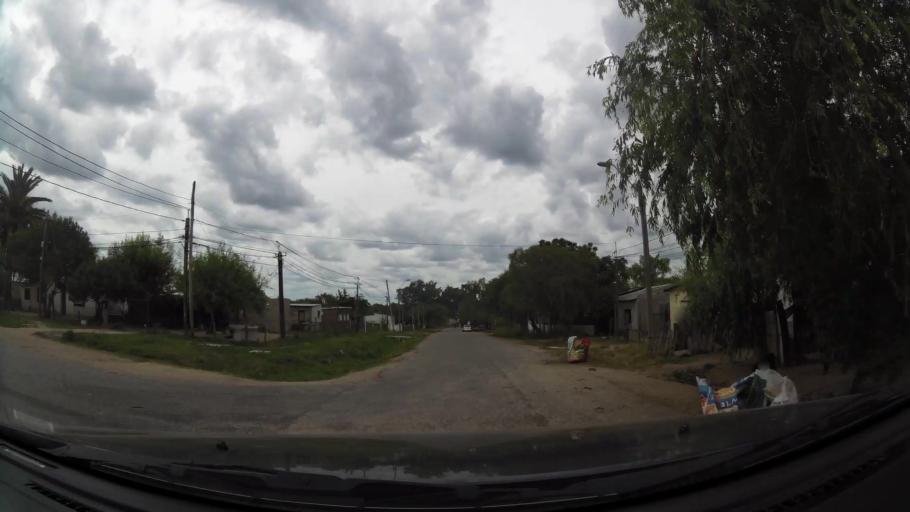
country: UY
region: Canelones
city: Las Piedras
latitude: -34.7143
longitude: -56.2066
